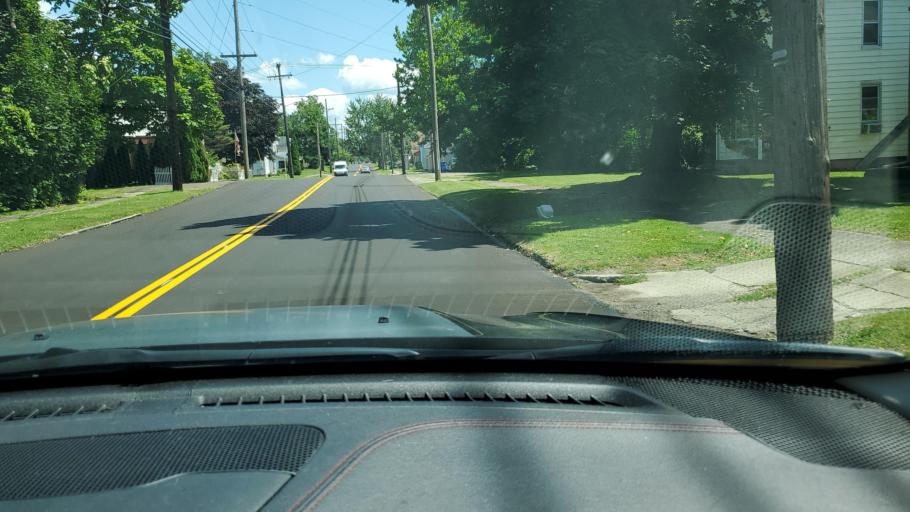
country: US
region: Ohio
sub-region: Trumbull County
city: Niles
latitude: 41.1805
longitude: -80.7737
